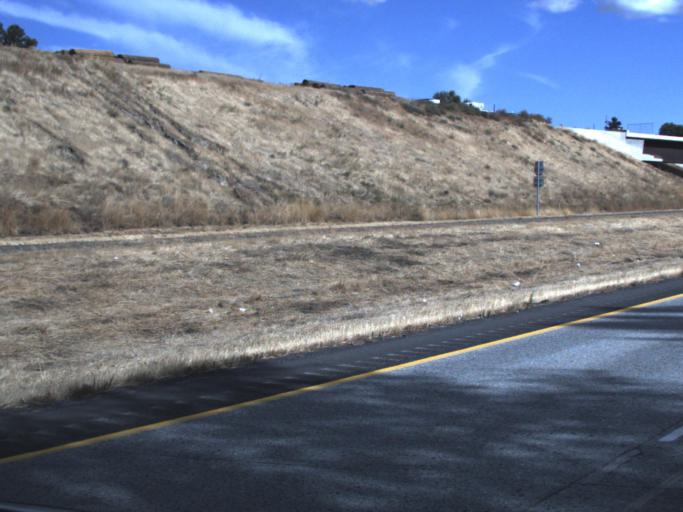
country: US
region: Washington
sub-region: Yakima County
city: Zillah
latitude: 46.3950
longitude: -120.2520
